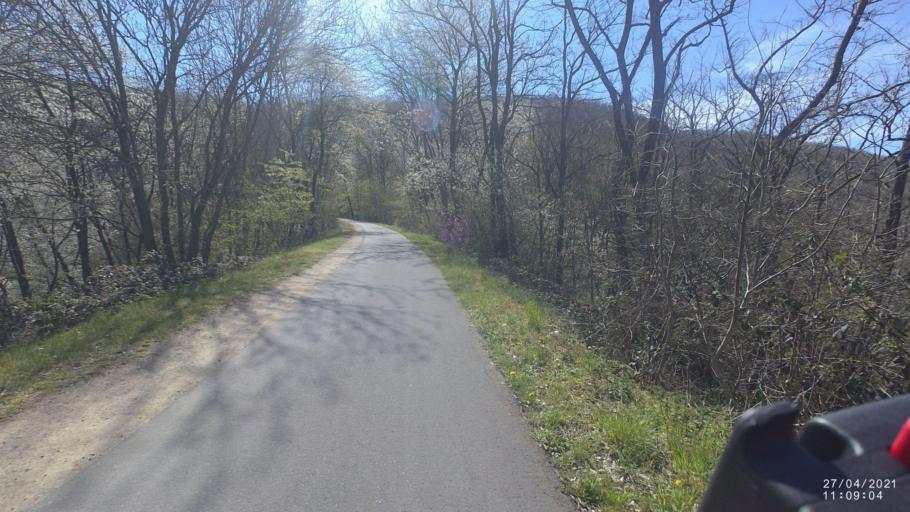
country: DE
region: Rheinland-Pfalz
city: Trimbs
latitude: 50.3167
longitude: 7.2718
